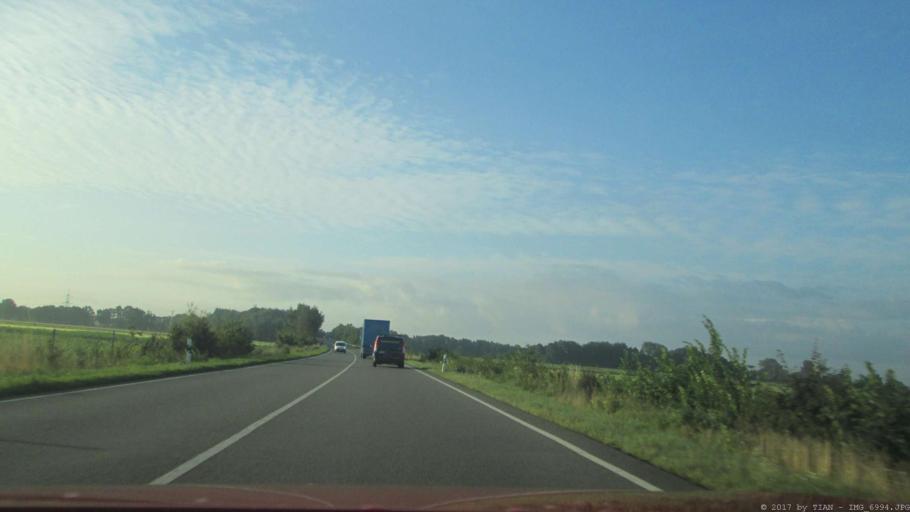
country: DE
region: Lower Saxony
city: Handorf
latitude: 53.3910
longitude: 10.3360
